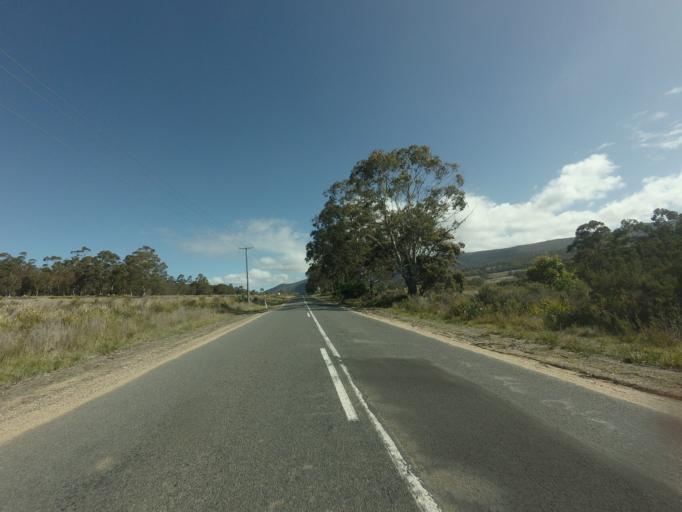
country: AU
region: Tasmania
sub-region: Break O'Day
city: St Helens
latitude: -41.6916
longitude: 148.2815
